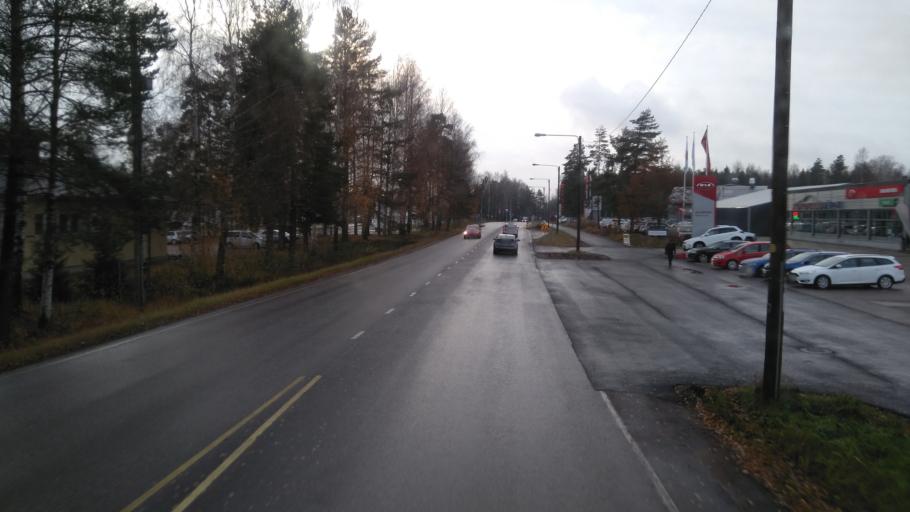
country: FI
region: Uusimaa
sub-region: Porvoo
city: Porvoo
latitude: 60.4027
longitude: 25.6877
